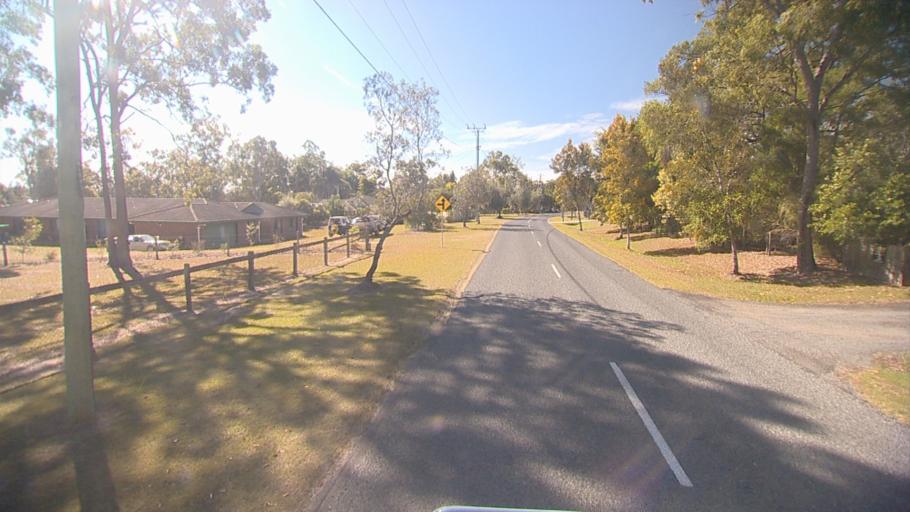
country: AU
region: Queensland
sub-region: Logan
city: North Maclean
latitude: -27.7431
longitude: 152.9553
